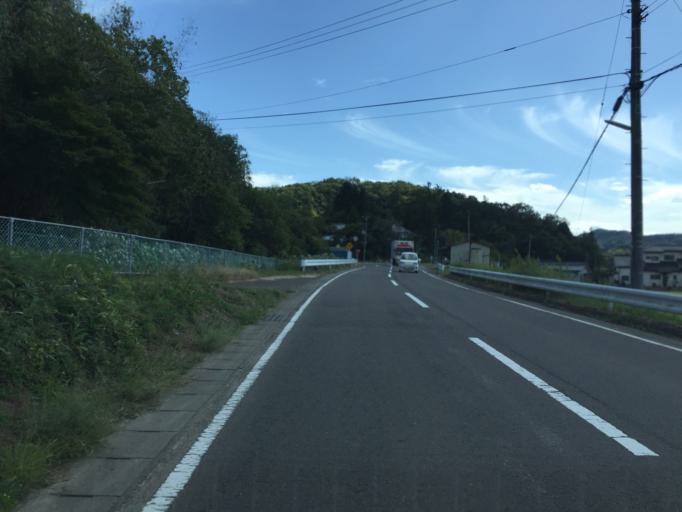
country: JP
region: Fukushima
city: Fukushima-shi
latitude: 37.7732
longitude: 140.5140
